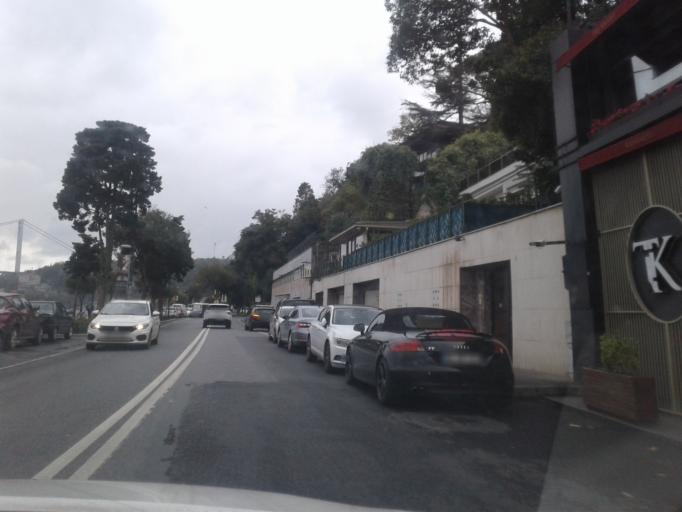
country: TR
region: Istanbul
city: Sisli
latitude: 41.1031
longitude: 29.0559
